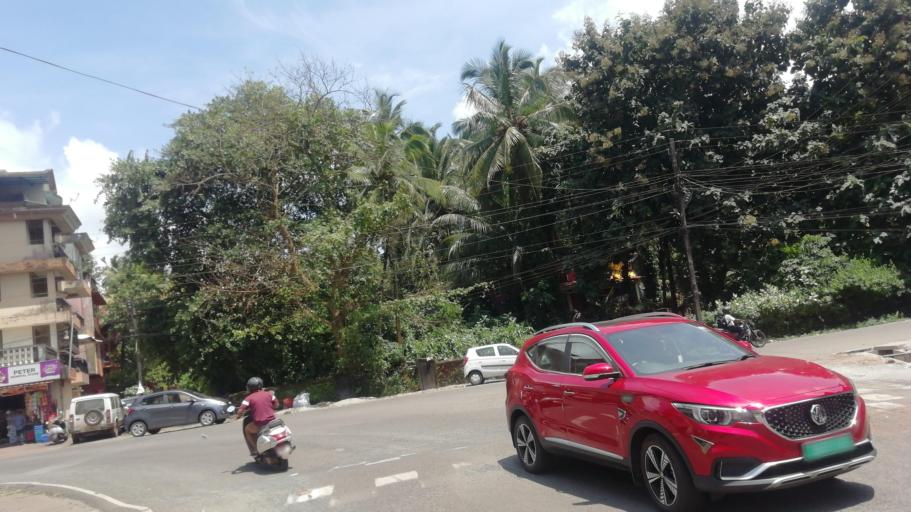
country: IN
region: Goa
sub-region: North Goa
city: Ponda
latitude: 15.3938
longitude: 74.0037
